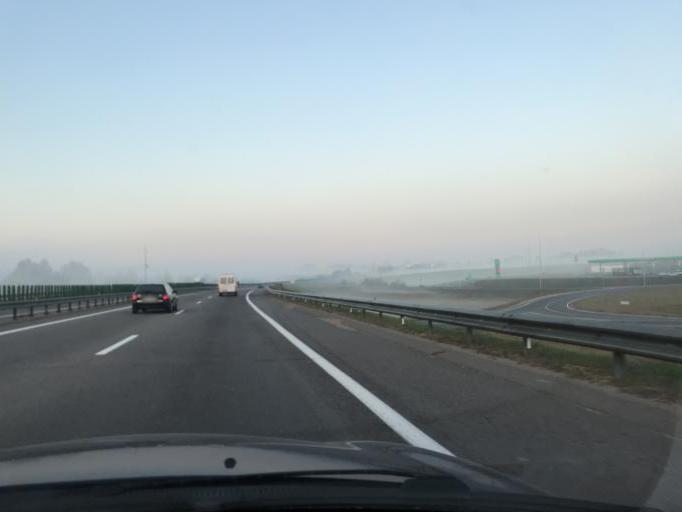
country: BY
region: Minsk
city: Khatsyezhyna
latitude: 53.9127
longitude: 27.2586
